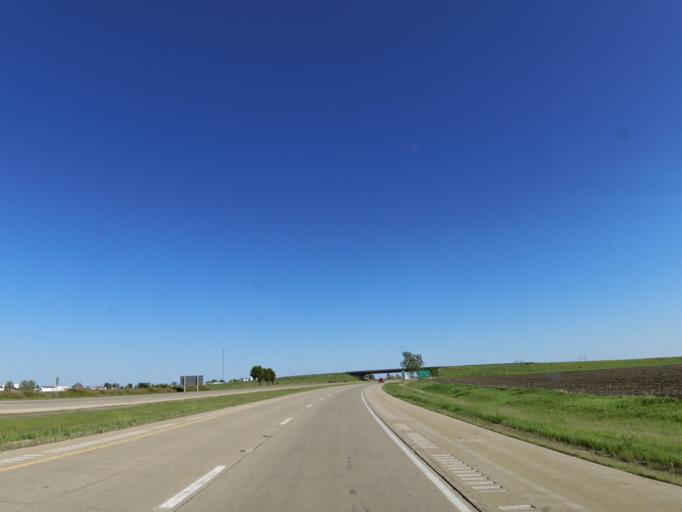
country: US
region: Illinois
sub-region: Marshall County
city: Wenona
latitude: 41.0457
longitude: -89.0585
